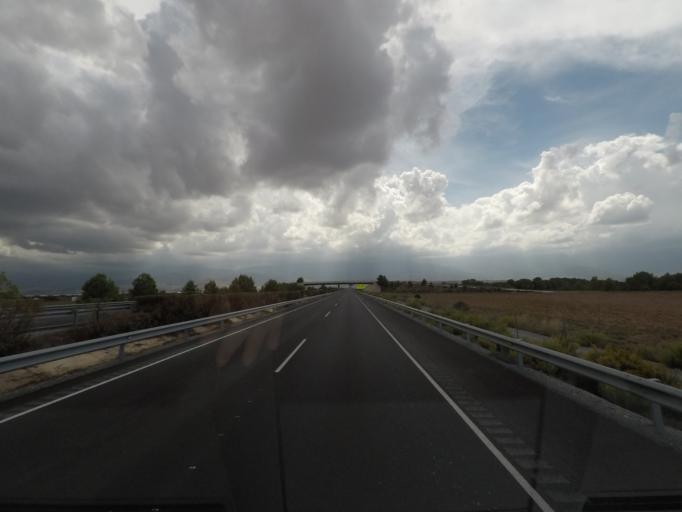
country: ES
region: Andalusia
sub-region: Provincia de Granada
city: Albunan
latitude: 37.2480
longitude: -3.0818
